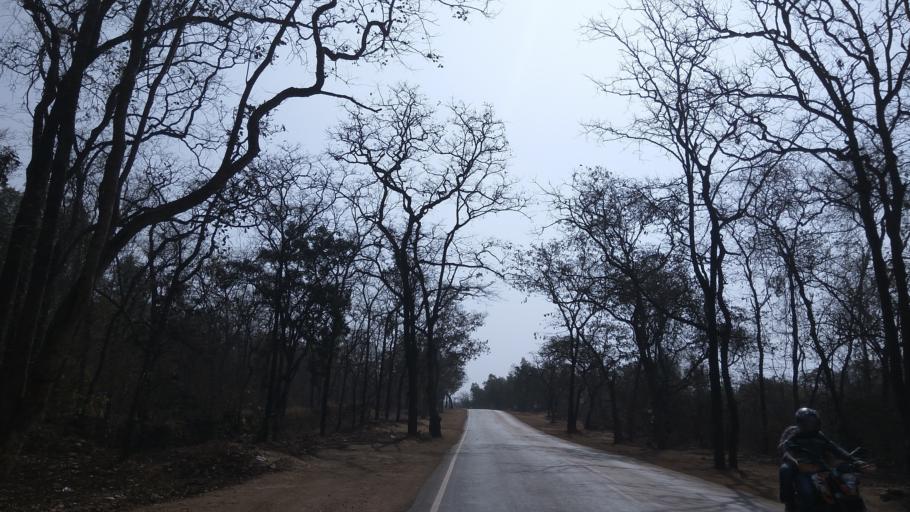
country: IN
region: Goa
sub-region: South Goa
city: Sanvordem
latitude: 15.3704
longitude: 74.1628
